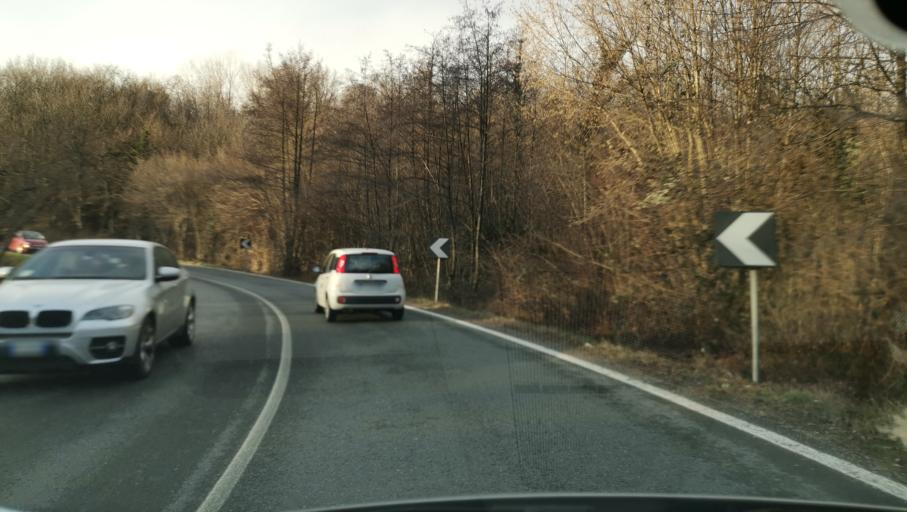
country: IT
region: Piedmont
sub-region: Provincia di Torino
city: Avigliana
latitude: 45.0590
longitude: 7.3799
